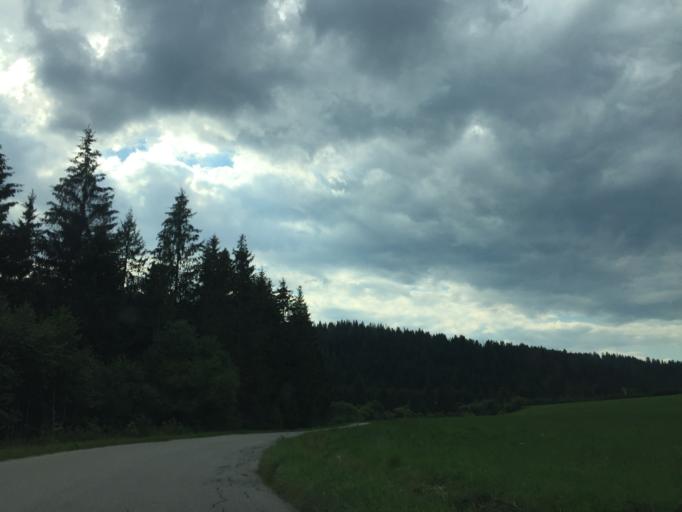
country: SK
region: Zilinsky
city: Namestovo
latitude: 49.3923
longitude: 19.3413
